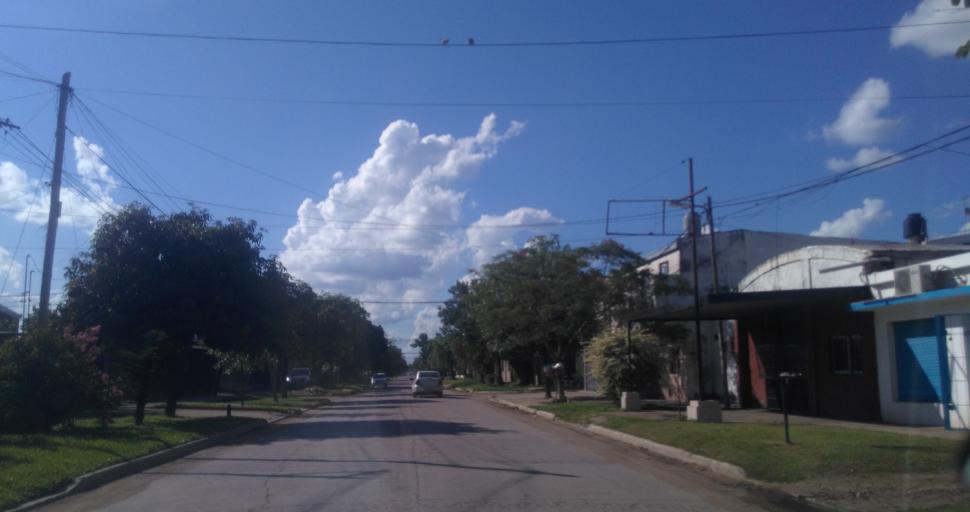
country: AR
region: Chaco
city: Resistencia
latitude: -27.4716
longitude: -58.9704
